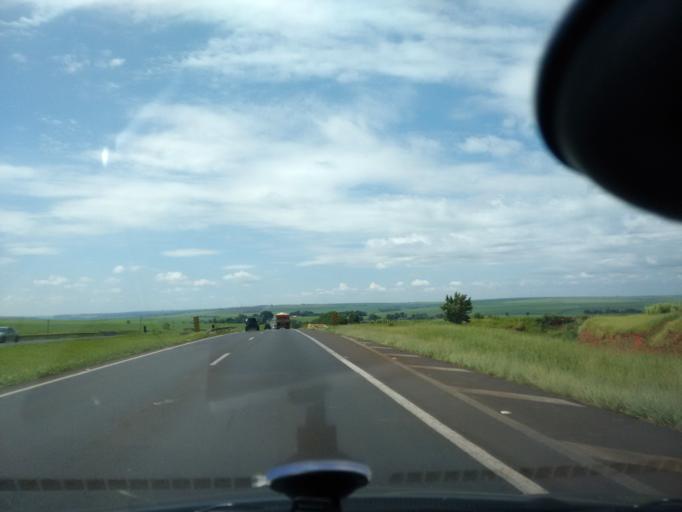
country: BR
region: Sao Paulo
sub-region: Araraquara
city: Araraquara
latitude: -21.8634
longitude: -48.1159
